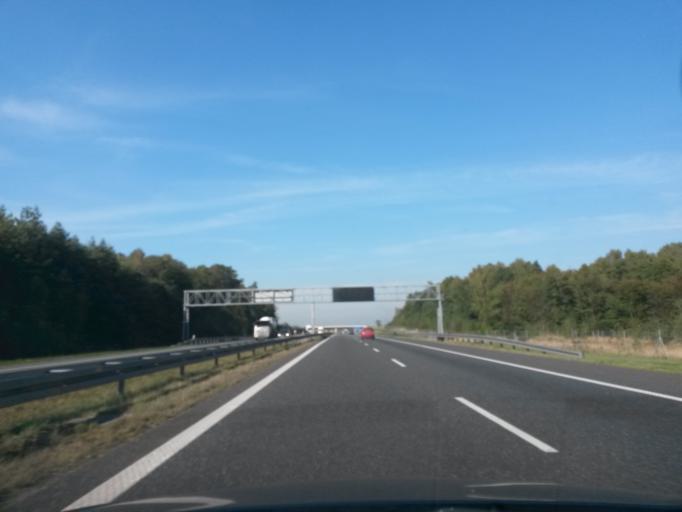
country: PL
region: Silesian Voivodeship
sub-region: Powiat gliwicki
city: Sosnicowice
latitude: 50.3334
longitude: 18.5454
